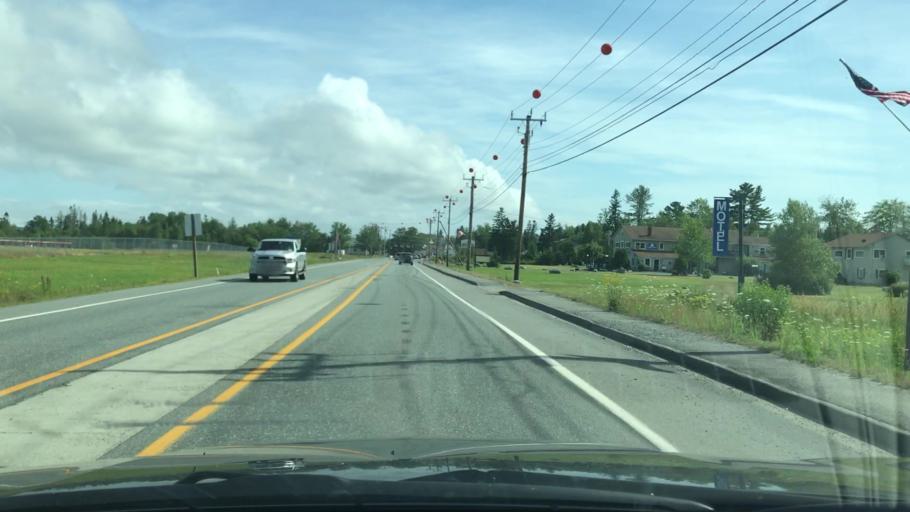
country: US
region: Maine
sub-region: Hancock County
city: Trenton
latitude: 44.4434
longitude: -68.3699
